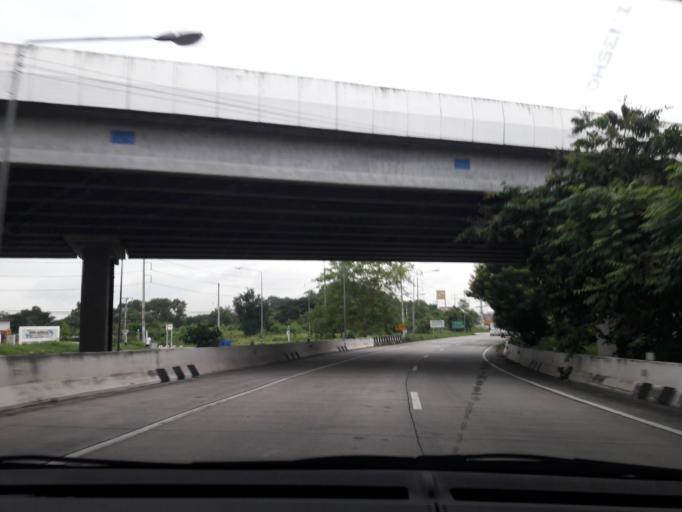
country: TH
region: Sara Buri
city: Saraburi
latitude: 14.5419
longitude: 100.9536
